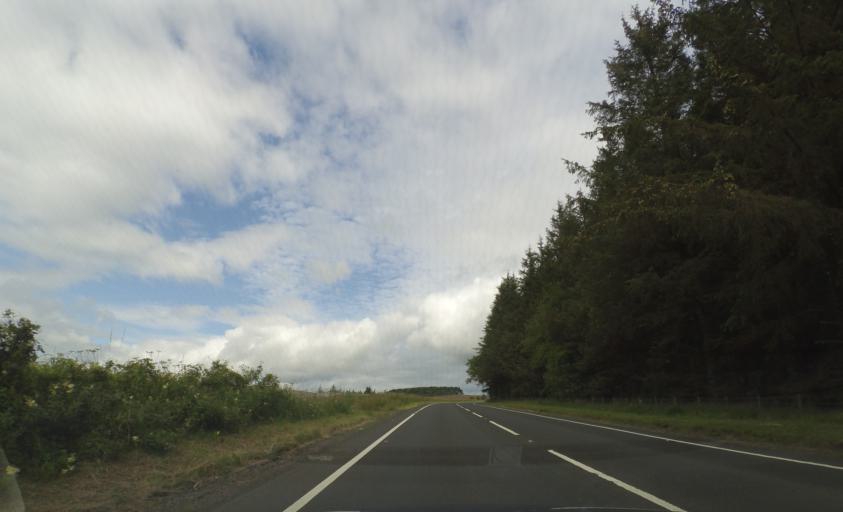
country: GB
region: Scotland
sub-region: The Scottish Borders
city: Selkirk
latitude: 55.5059
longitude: -2.8409
